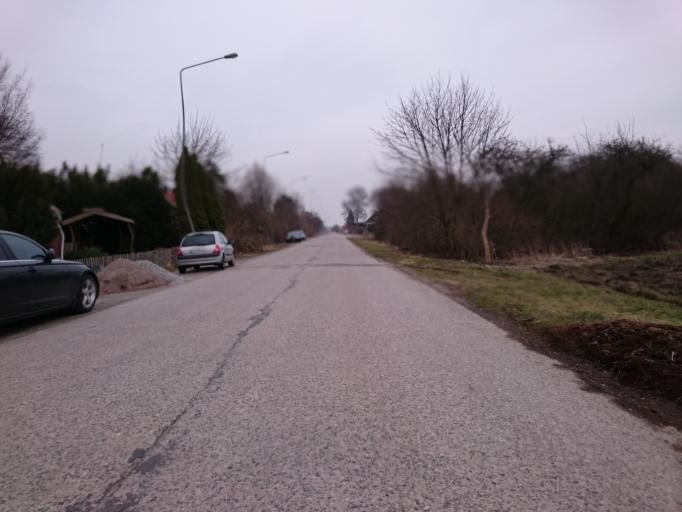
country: SE
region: Skane
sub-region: Staffanstorps Kommun
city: Hjaerup
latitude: 55.6731
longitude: 13.1699
